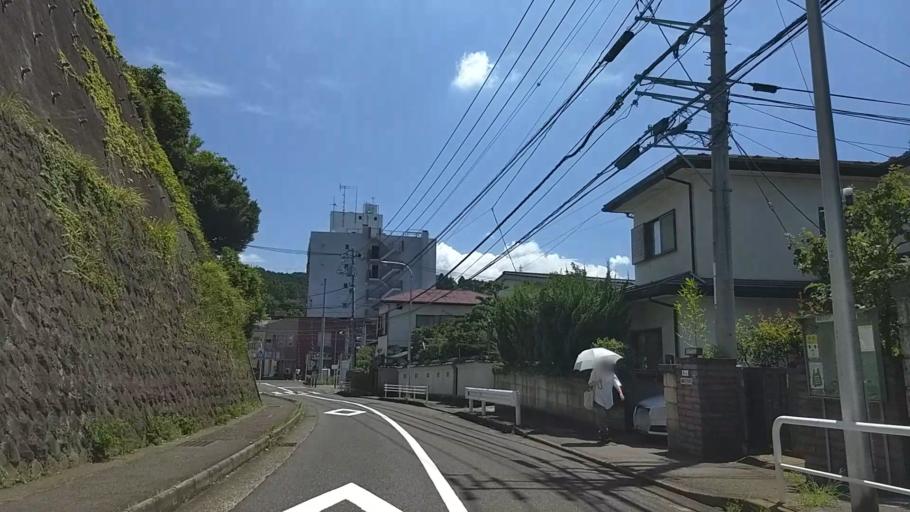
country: JP
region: Kanagawa
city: Zushi
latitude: 35.2998
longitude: 139.6006
